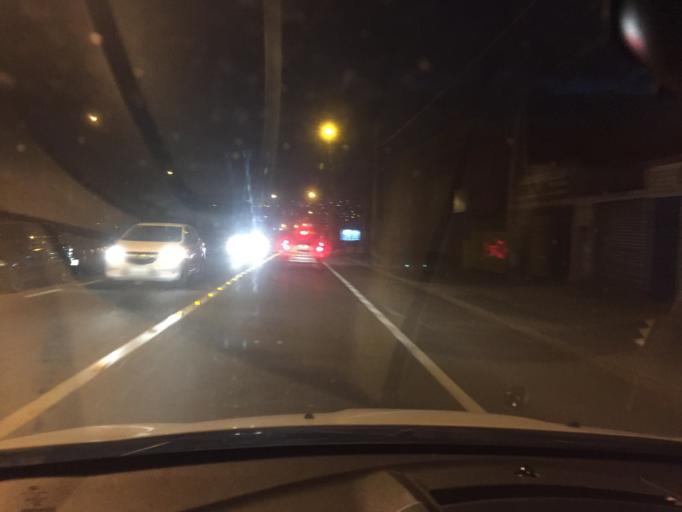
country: BR
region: Sao Paulo
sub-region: Campo Limpo Paulista
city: Campo Limpo Paulista
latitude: -23.2059
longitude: -46.8014
